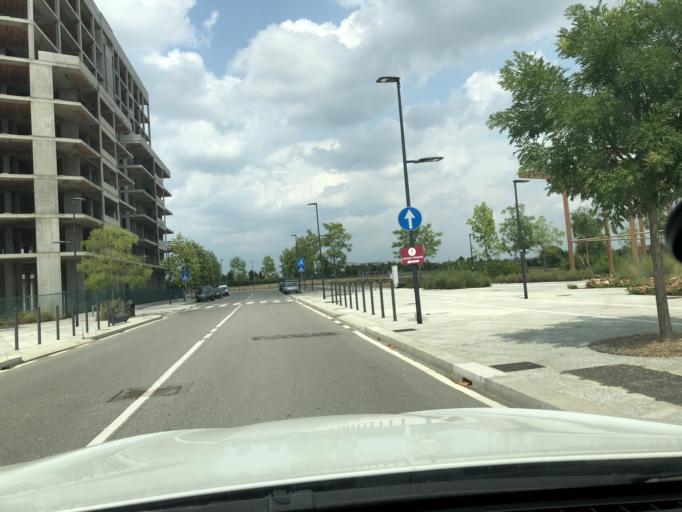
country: IT
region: Lombardy
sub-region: Citta metropolitana di Milano
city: Pero
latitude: 45.5102
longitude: 9.1014
